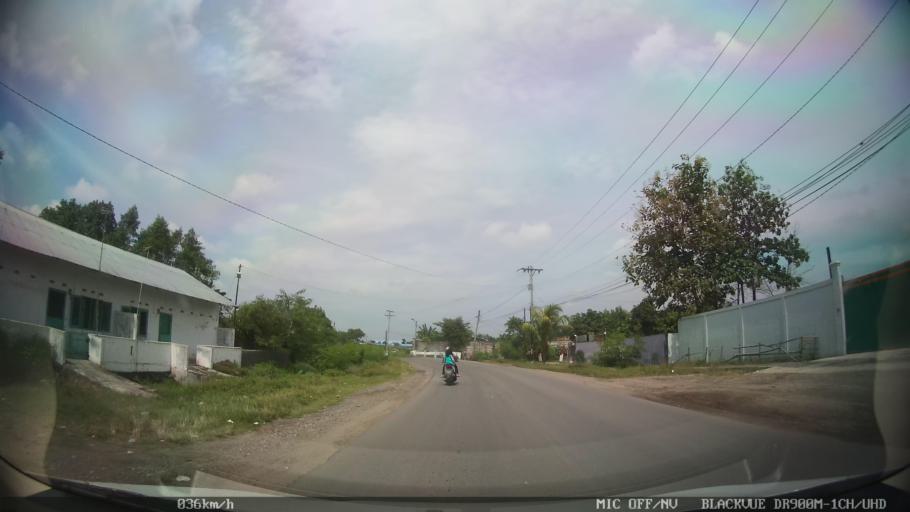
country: ID
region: North Sumatra
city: Medan
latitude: 3.6505
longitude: 98.7146
